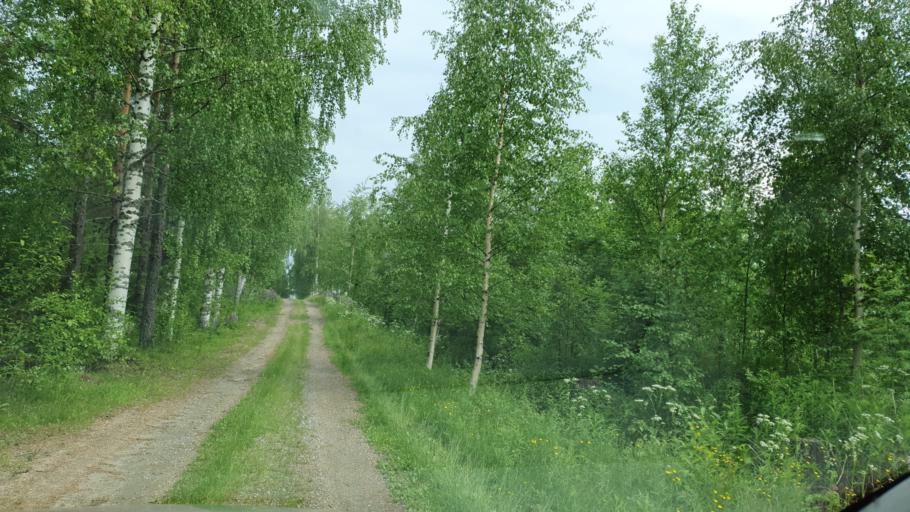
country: FI
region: Kainuu
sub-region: Kehys-Kainuu
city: Kuhmo
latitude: 64.3173
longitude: 29.8824
